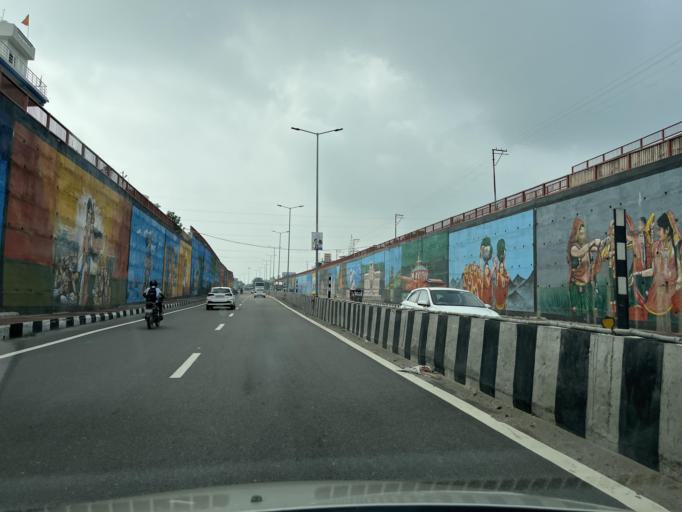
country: IN
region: Uttarakhand
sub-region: Dehradun
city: Raiwala
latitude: 30.0404
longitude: 78.2103
